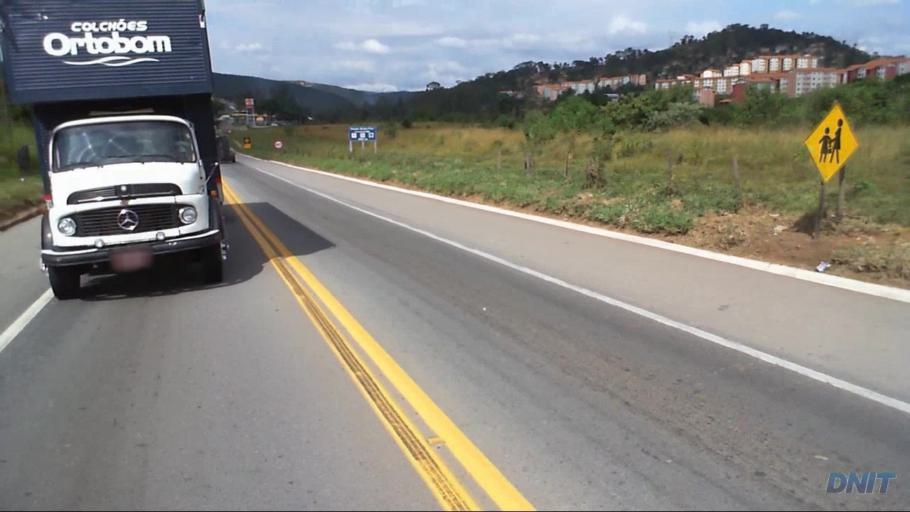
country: BR
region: Minas Gerais
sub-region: Santa Luzia
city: Santa Luzia
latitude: -19.8385
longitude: -43.8801
